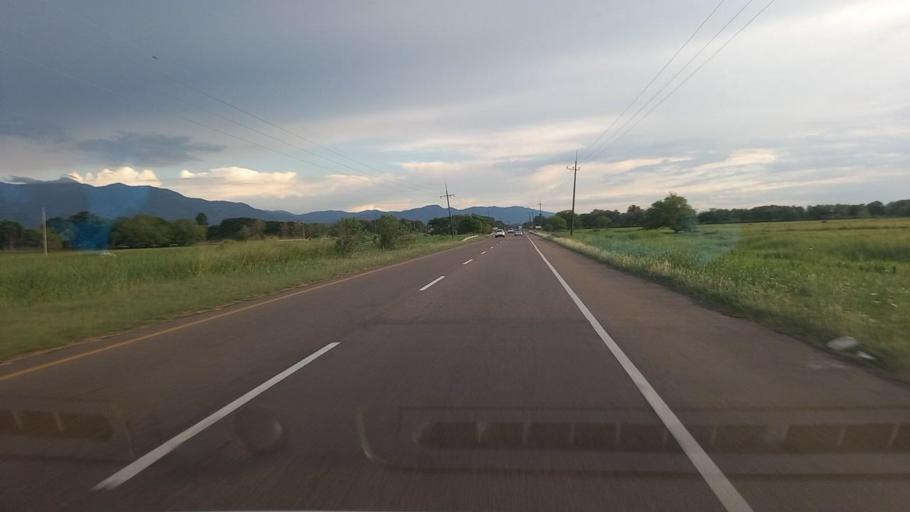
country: CO
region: Cundinamarca
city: Puerto Salgar
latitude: 5.5837
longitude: -74.6236
